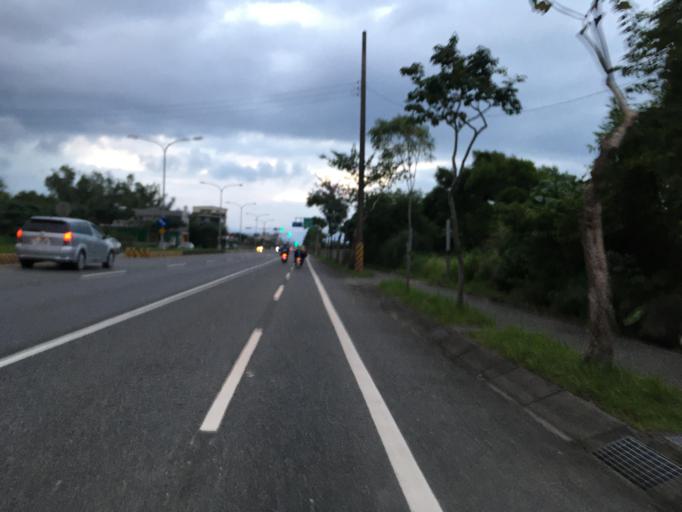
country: TW
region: Taiwan
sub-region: Yilan
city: Yilan
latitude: 24.6181
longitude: 121.8453
